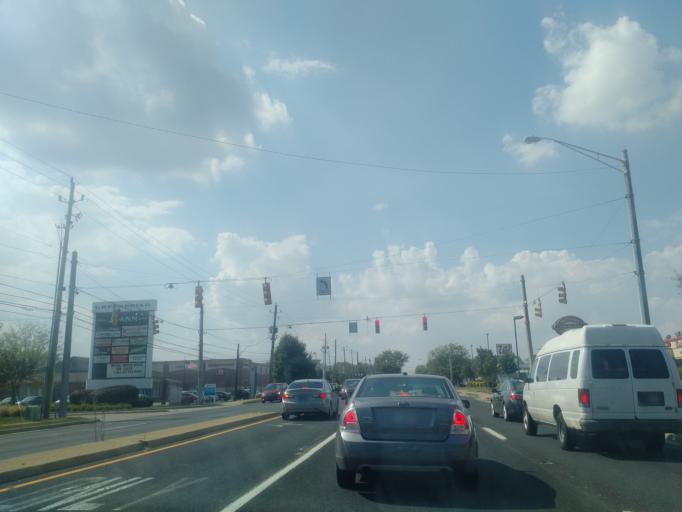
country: US
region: Indiana
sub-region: Marion County
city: Meridian Hills
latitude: 39.9123
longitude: -86.1810
